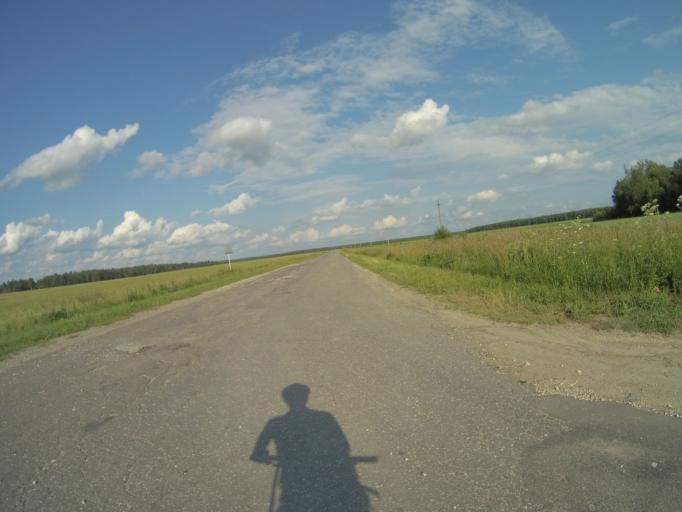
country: RU
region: Vladimir
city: Orgtrud
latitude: 56.3446
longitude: 40.6982
